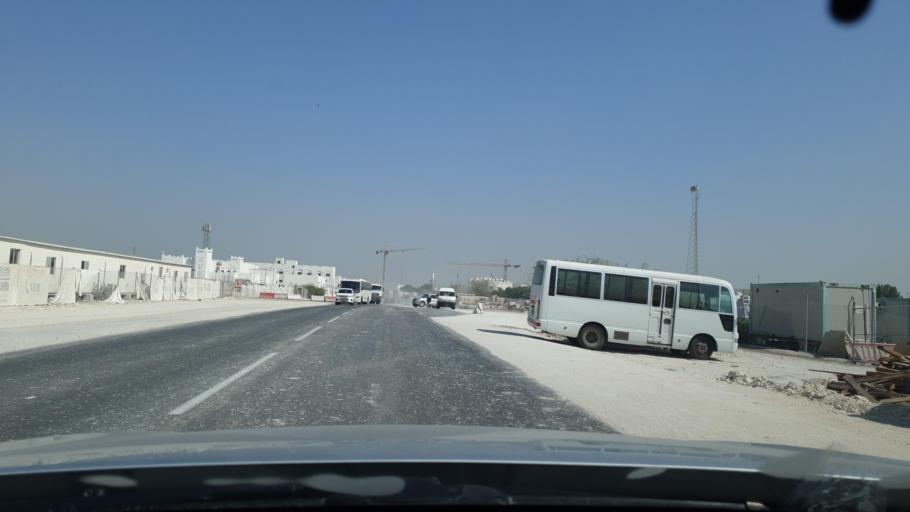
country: QA
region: Baladiyat ad Dawhah
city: Doha
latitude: 25.2284
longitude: 51.5213
